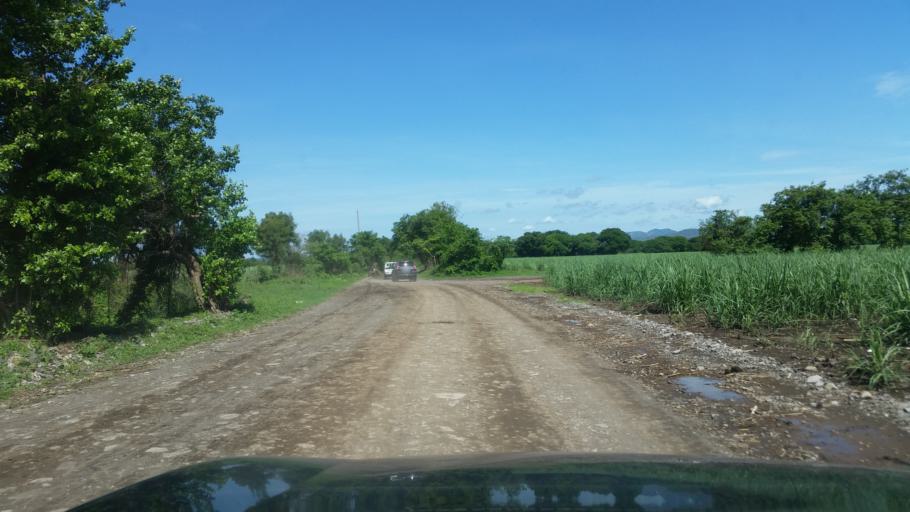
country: NI
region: Chinandega
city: Puerto Morazan
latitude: 12.7734
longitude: -87.1195
